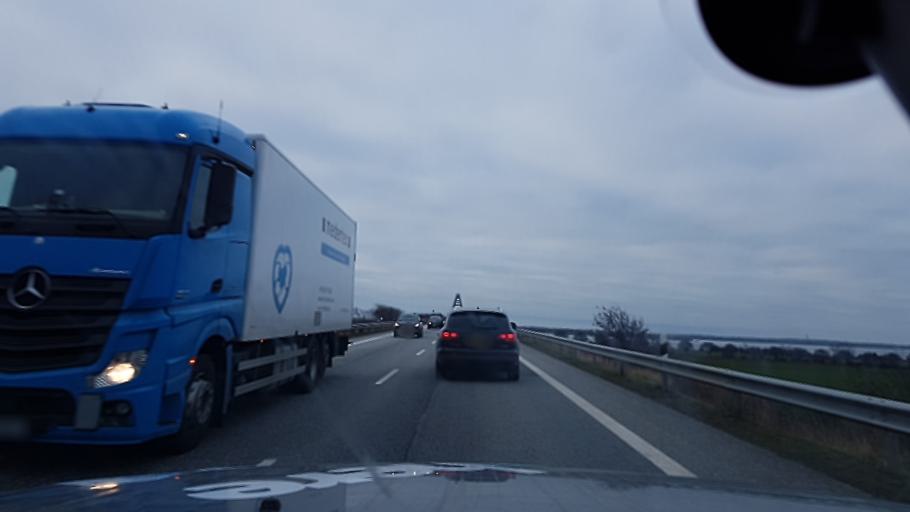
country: DE
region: Schleswig-Holstein
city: Grossenbrode
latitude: 54.4120
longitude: 11.1190
